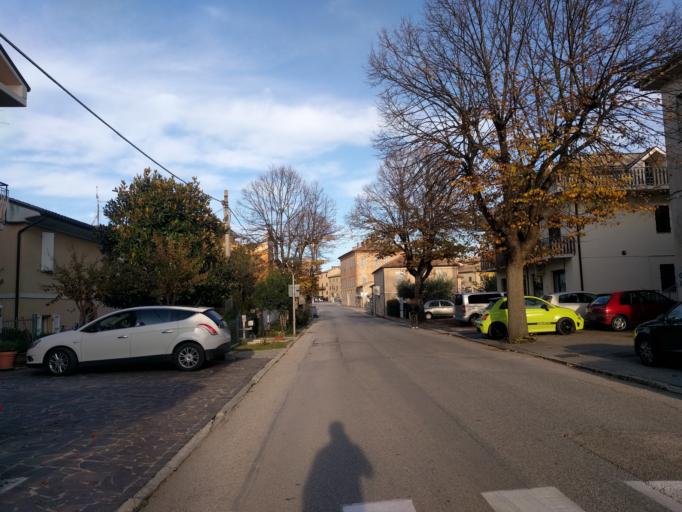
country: IT
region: The Marches
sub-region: Provincia di Ancona
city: Ostra
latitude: 43.6110
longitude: 13.1543
